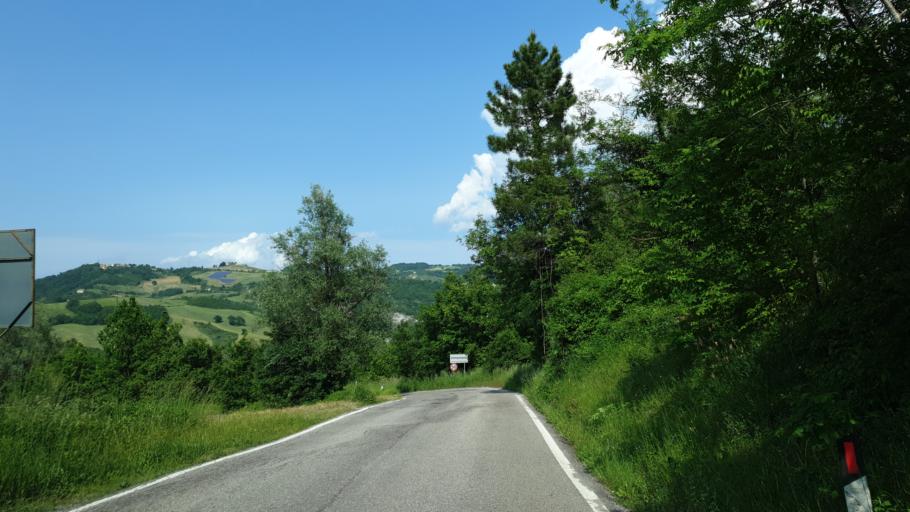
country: IT
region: Emilia-Romagna
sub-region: Forli-Cesena
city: Sarsina
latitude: 43.9146
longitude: 12.1704
